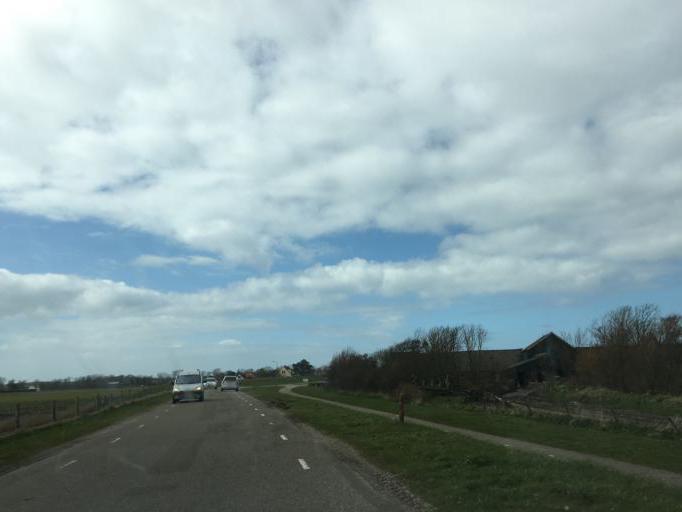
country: NL
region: North Holland
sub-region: Gemeente Schagen
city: Schagen
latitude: 52.8573
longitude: 4.7288
